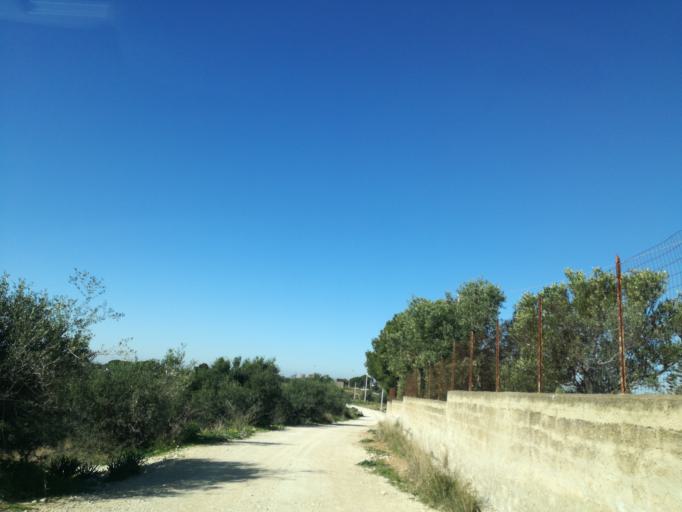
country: IT
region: Sicily
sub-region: Provincia di Caltanissetta
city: Niscemi
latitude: 37.0551
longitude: 14.3628
